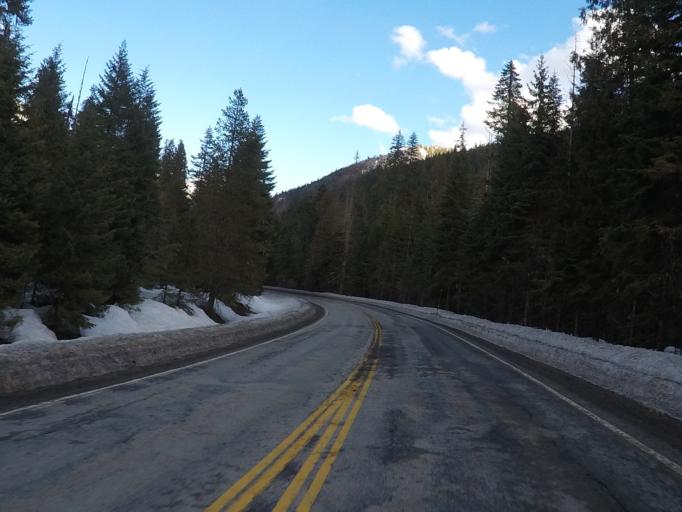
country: US
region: Montana
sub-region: Ravalli County
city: Hamilton
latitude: 46.5076
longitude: -114.7764
